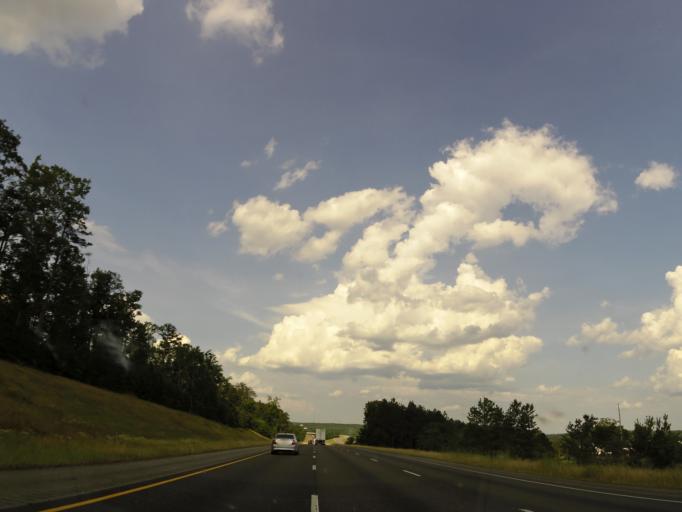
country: US
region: Alabama
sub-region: Tuscaloosa County
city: Vance
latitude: 33.1885
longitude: -87.2682
